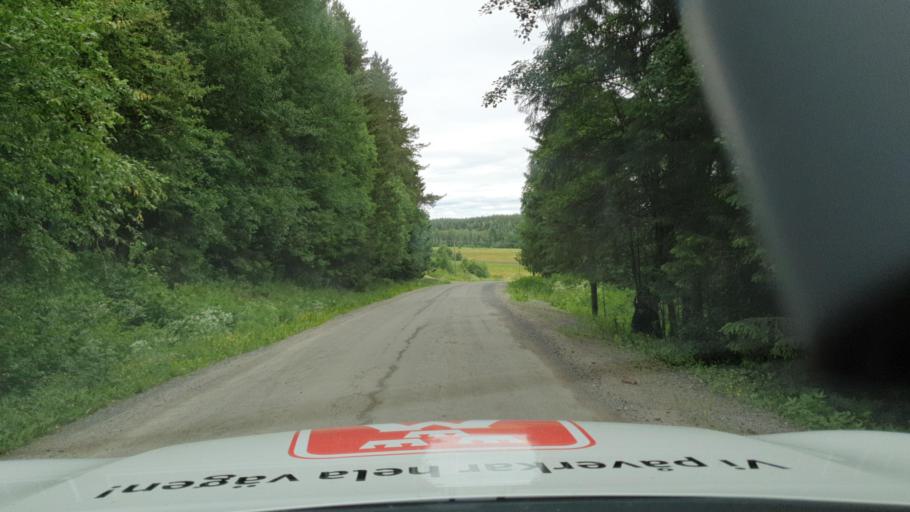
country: SE
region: Vaesterbotten
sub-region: Nordmalings Kommun
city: Nordmaling
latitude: 63.6419
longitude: 19.4207
